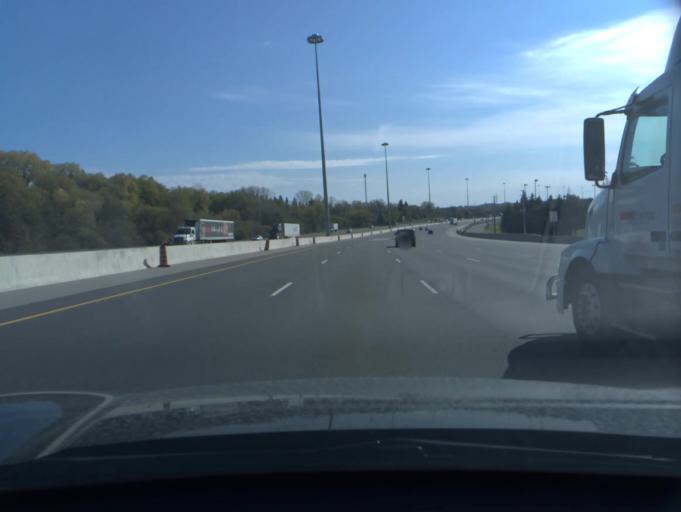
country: CA
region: Ontario
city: North Perth
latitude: 43.8225
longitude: -81.0001
